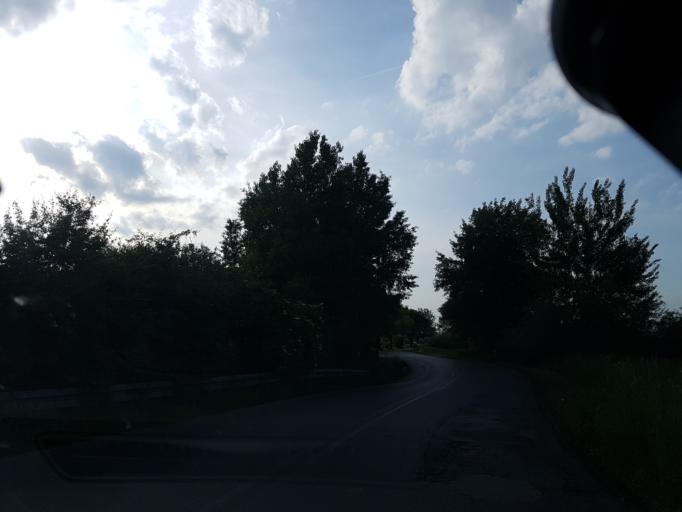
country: PL
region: Lower Silesian Voivodeship
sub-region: Powiat wroclawski
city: Kobierzyce
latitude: 50.9137
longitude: 16.9912
